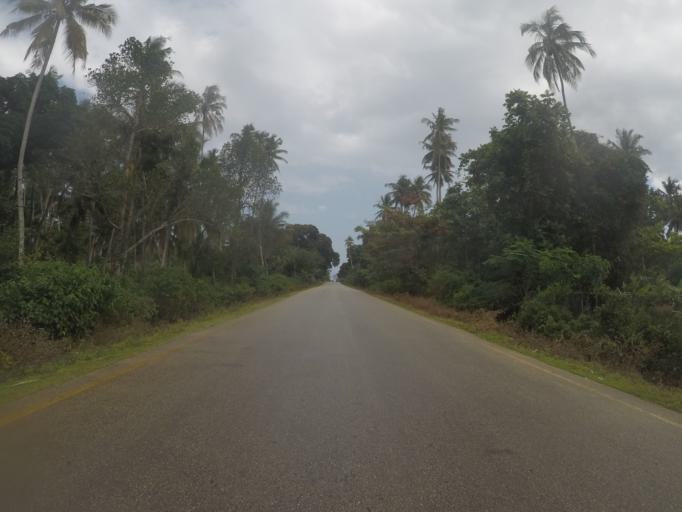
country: TZ
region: Zanzibar North
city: Mkokotoni
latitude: -5.9960
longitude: 39.1940
